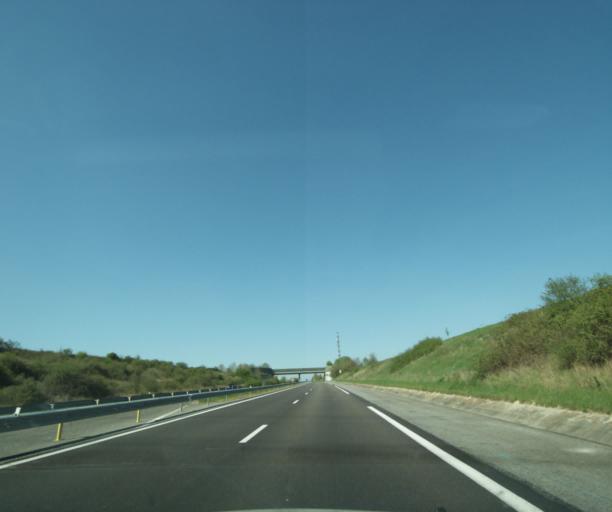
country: FR
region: Bourgogne
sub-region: Departement de la Nievre
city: Cosne-Cours-sur-Loire
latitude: 47.4573
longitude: 2.9479
